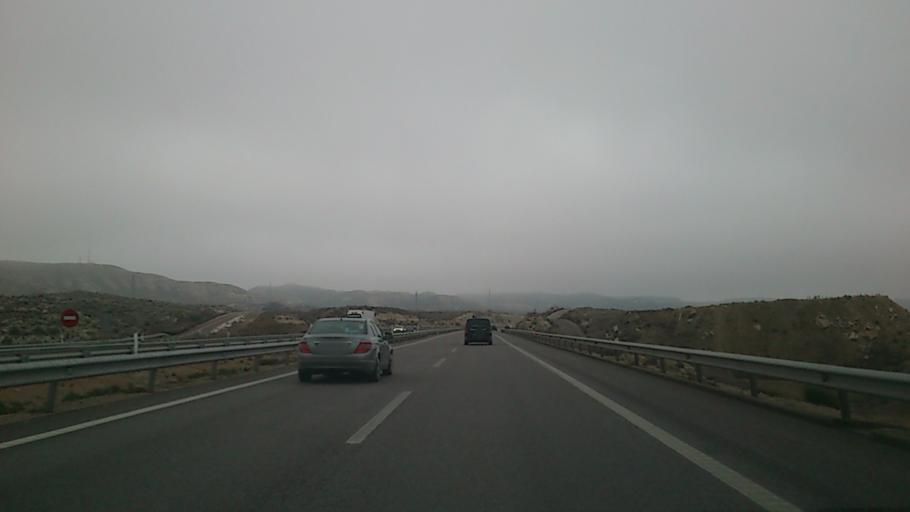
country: ES
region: Aragon
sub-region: Provincia de Zaragoza
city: Muel
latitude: 41.5502
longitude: -1.1595
